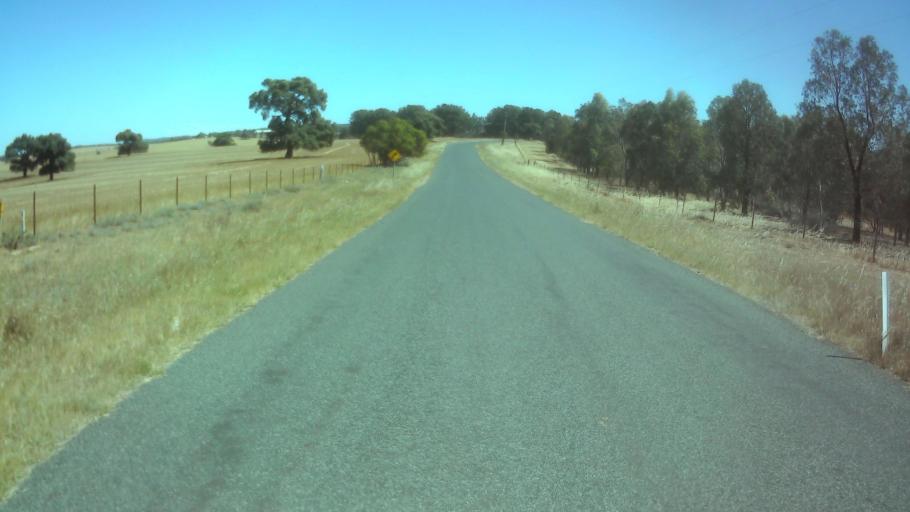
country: AU
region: New South Wales
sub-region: Weddin
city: Grenfell
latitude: -33.9572
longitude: 148.4003
